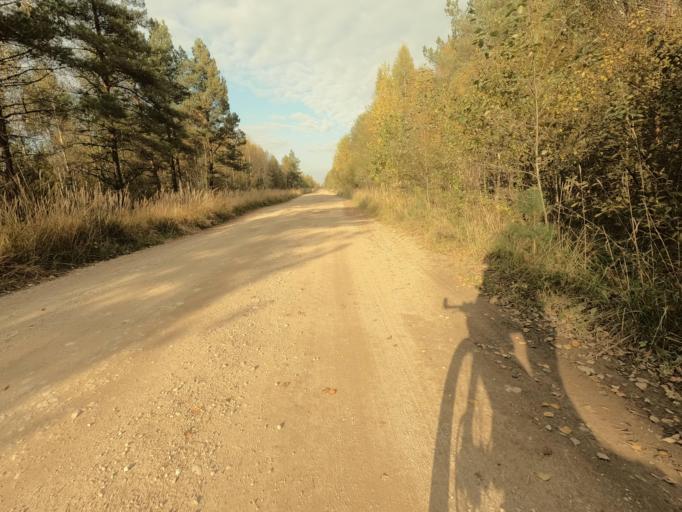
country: RU
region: Novgorod
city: Volkhovskiy
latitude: 58.8999
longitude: 31.0326
